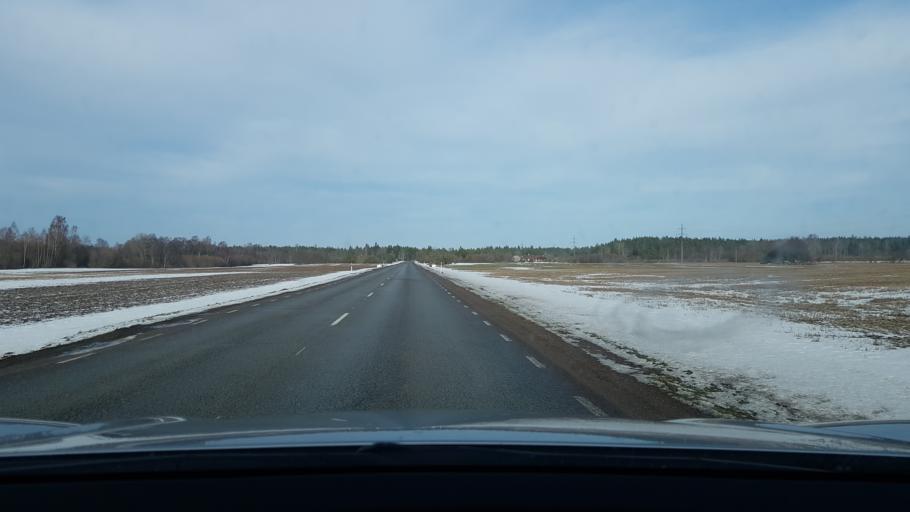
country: EE
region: Saare
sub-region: Kuressaare linn
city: Kuressaare
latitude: 58.3126
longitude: 22.5434
